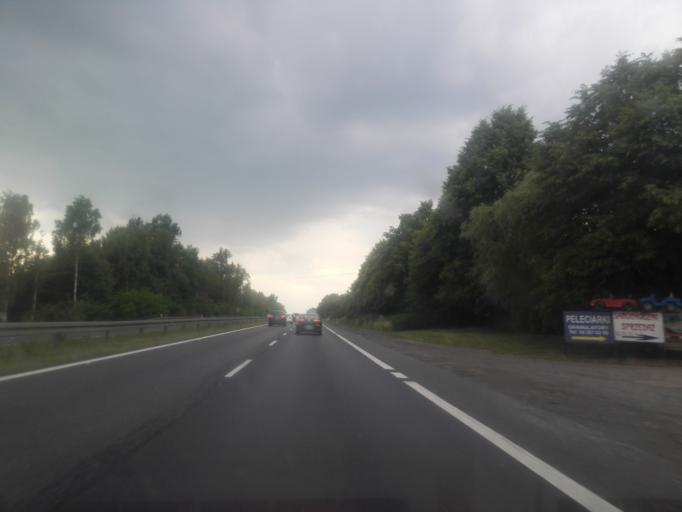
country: PL
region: Silesian Voivodeship
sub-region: Powiat czestochowski
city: Huta Stara B
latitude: 50.7395
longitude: 19.1577
